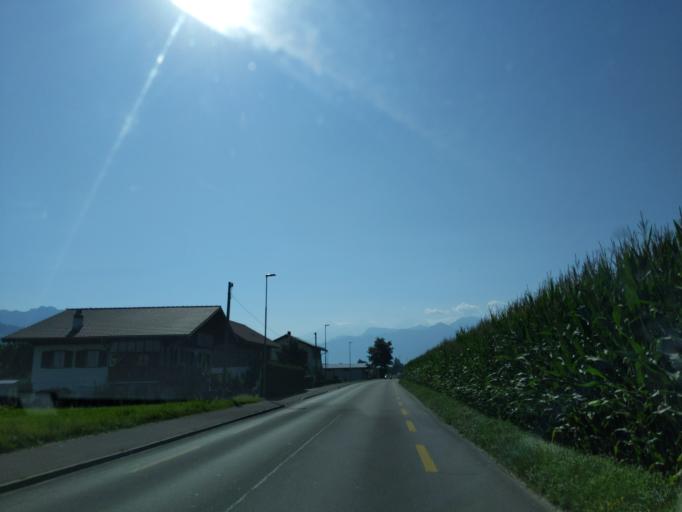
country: CH
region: Bern
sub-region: Thun District
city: Thun
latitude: 46.7362
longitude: 7.6044
